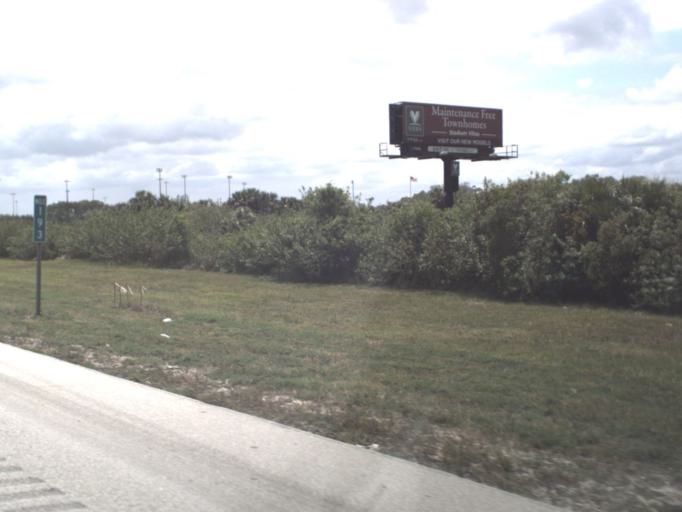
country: US
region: Florida
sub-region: Brevard County
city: Rockledge
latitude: 28.2599
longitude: -80.7273
